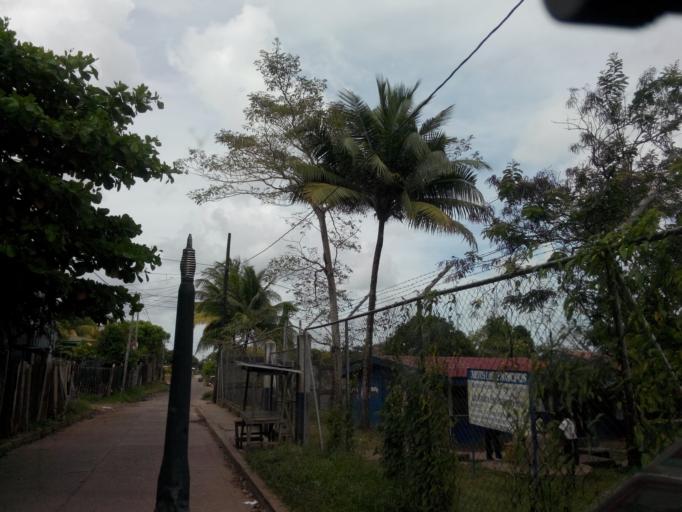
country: NI
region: Atlantico Sur
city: Bluefields
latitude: 11.9975
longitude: -83.7670
